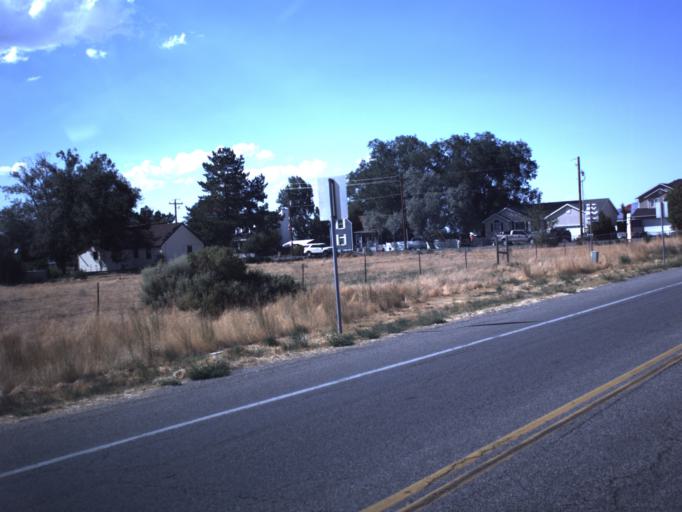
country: US
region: Utah
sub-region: Tooele County
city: Grantsville
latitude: 40.5987
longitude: -112.4260
